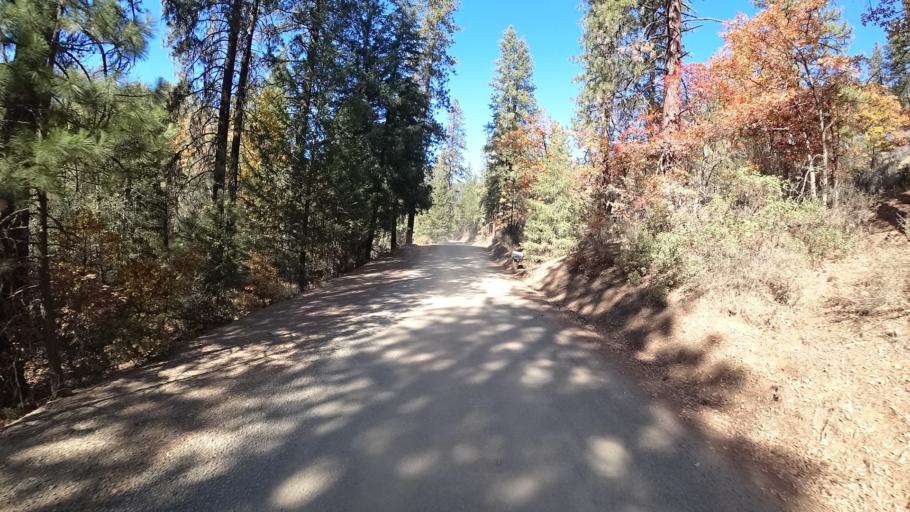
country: US
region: California
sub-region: Siskiyou County
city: Yreka
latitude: 41.6871
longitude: -122.8545
